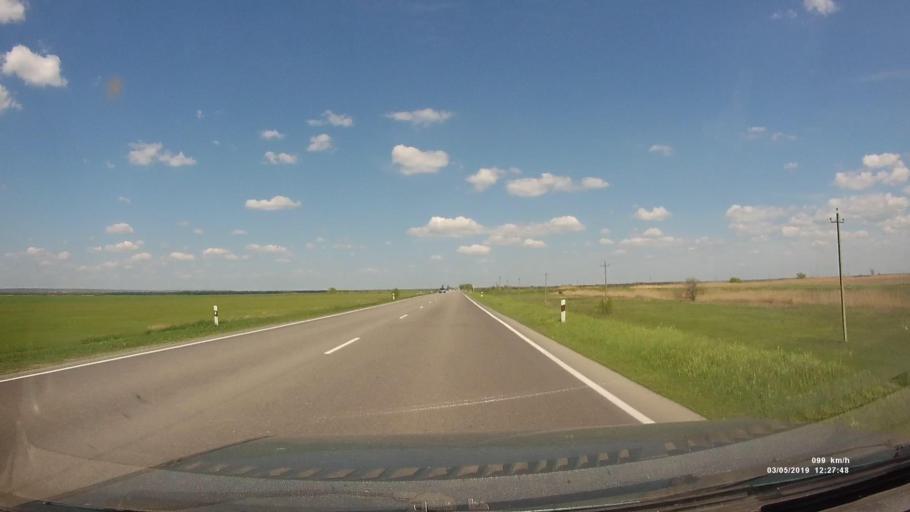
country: RU
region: Rostov
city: Semikarakorsk
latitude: 47.4640
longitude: 40.7234
